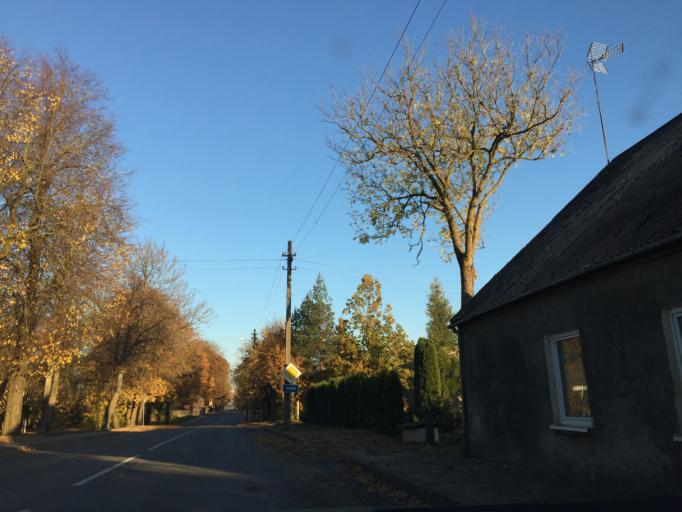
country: LT
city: Vieksniai
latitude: 56.3814
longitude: 22.5596
